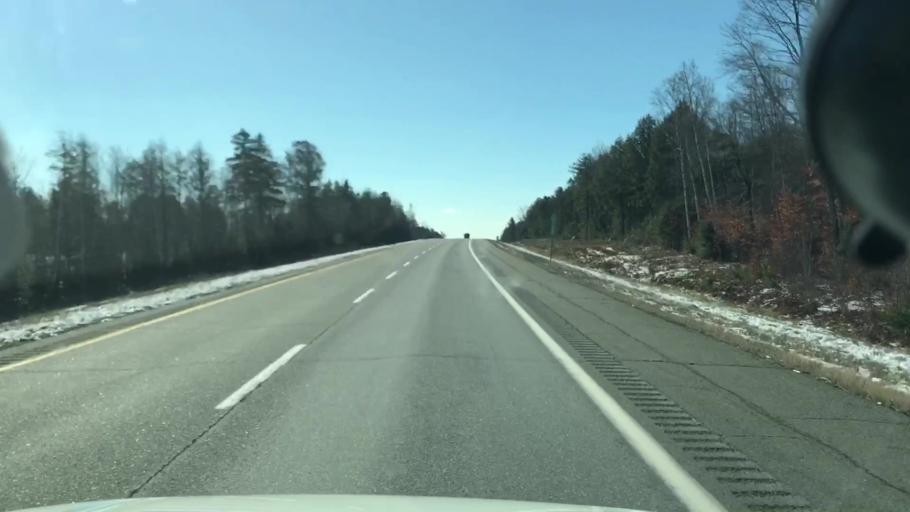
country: US
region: Maine
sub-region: Penobscot County
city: Howland
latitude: 45.2842
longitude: -68.6693
